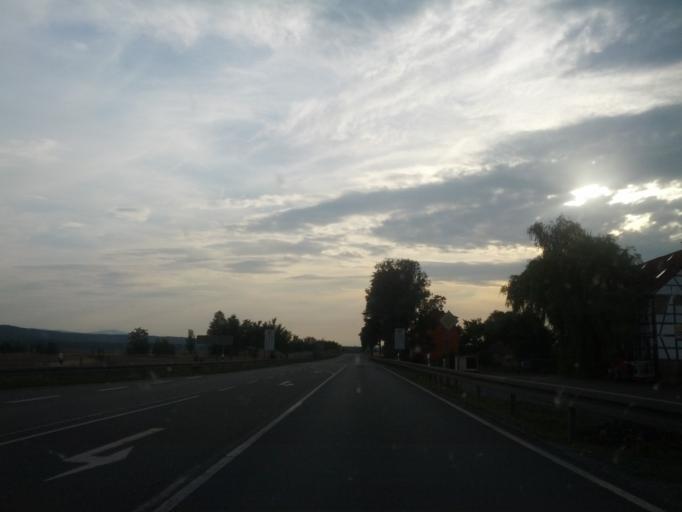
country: DE
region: Thuringia
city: Grabsleben
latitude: 50.9460
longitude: 10.8214
